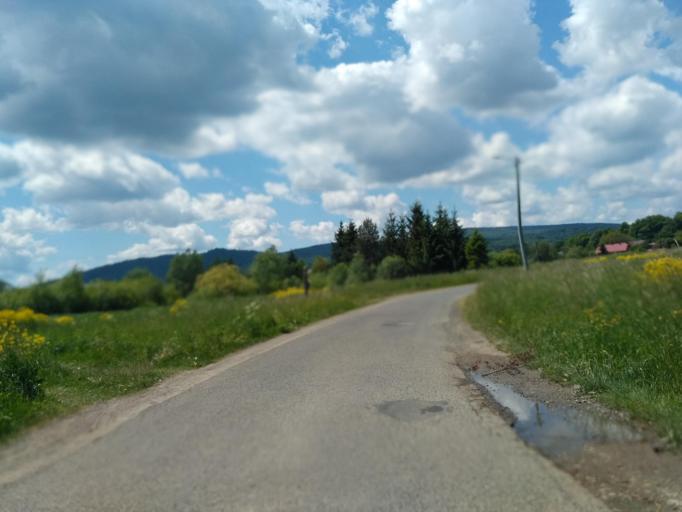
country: PL
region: Subcarpathian Voivodeship
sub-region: Powiat krosnienski
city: Dukla
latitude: 49.5610
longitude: 21.6944
